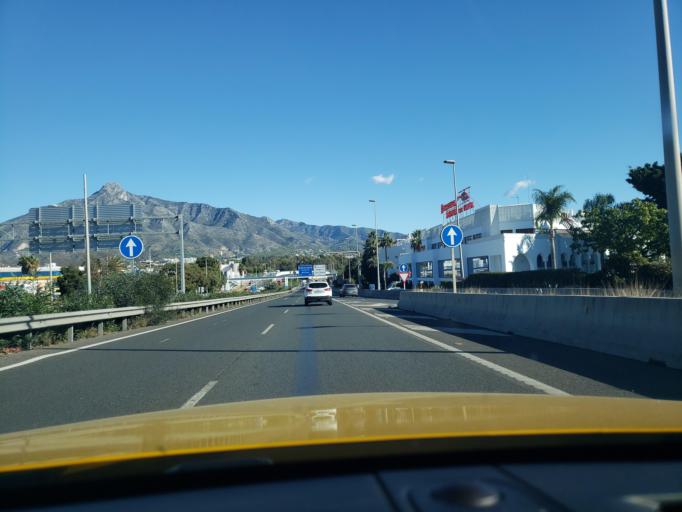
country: ES
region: Andalusia
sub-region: Provincia de Malaga
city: Marbella
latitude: 36.4933
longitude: -4.9517
